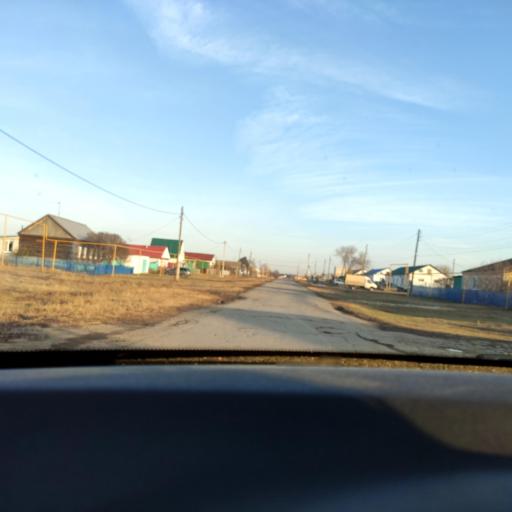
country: RU
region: Samara
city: Krasnoarmeyskoye
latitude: 52.9011
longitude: 50.0317
